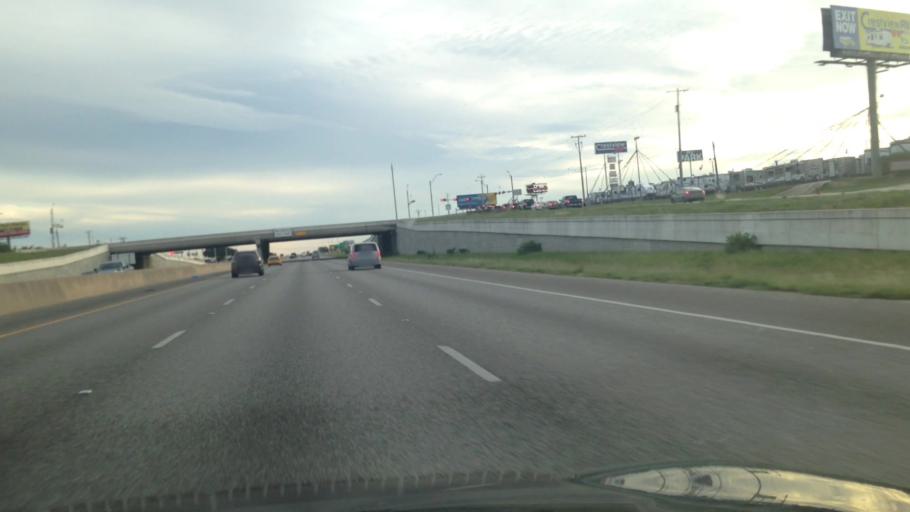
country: US
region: Texas
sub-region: Hays County
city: Buda
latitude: 30.0813
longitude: -97.8231
